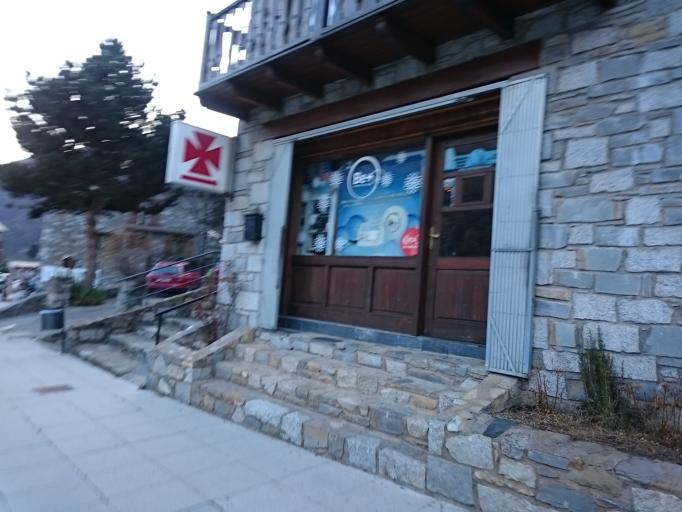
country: ES
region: Aragon
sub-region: Provincia de Huesca
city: Bonansa
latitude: 42.5052
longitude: 0.8044
